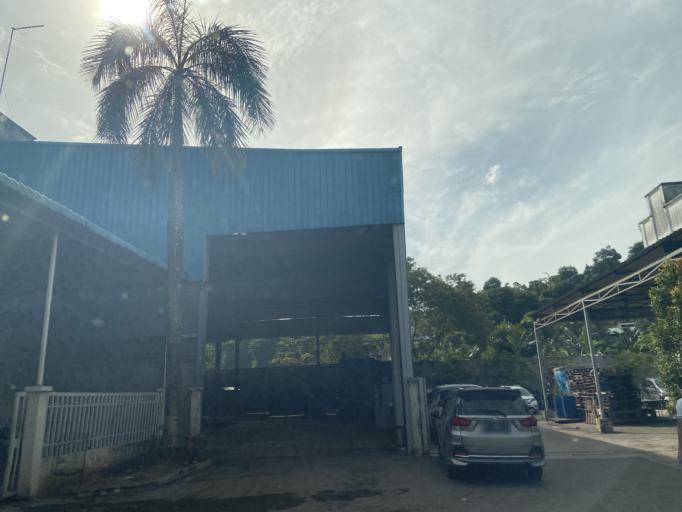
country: SG
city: Singapore
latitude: 1.1483
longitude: 104.0206
